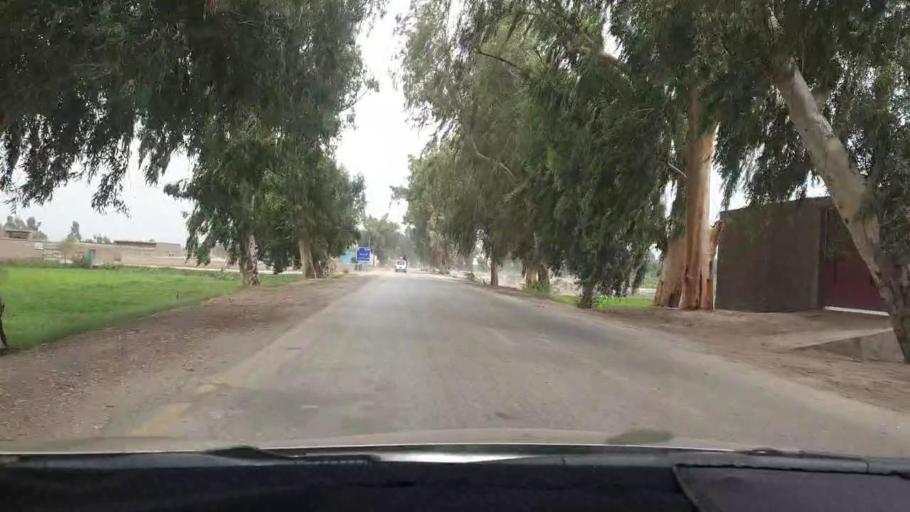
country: PK
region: Sindh
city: Naudero
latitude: 27.6595
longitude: 68.3447
